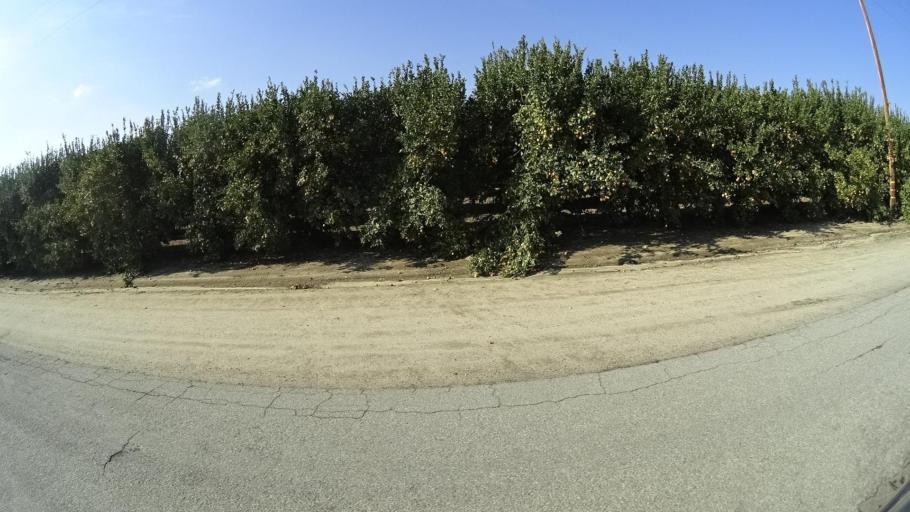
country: US
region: California
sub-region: Kern County
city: Arvin
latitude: 35.2909
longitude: -118.7708
